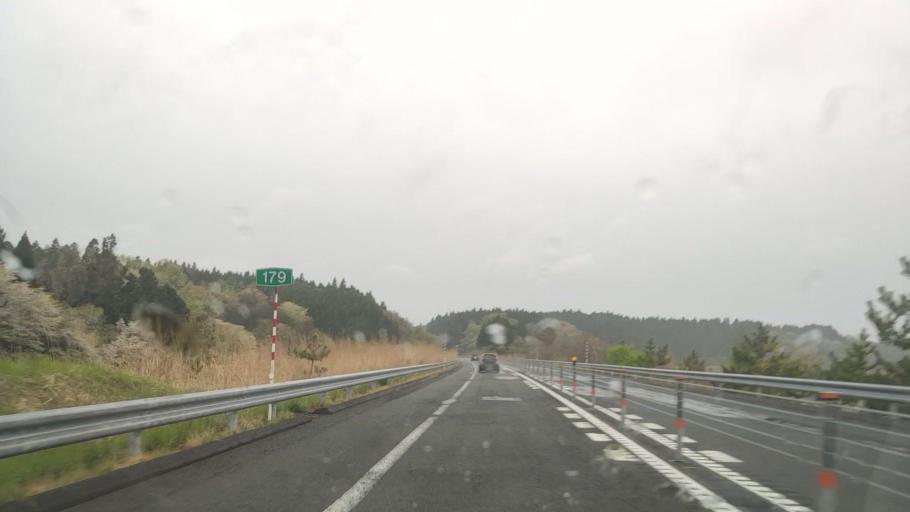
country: JP
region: Akita
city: Noshiromachi
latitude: 40.1920
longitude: 140.1101
